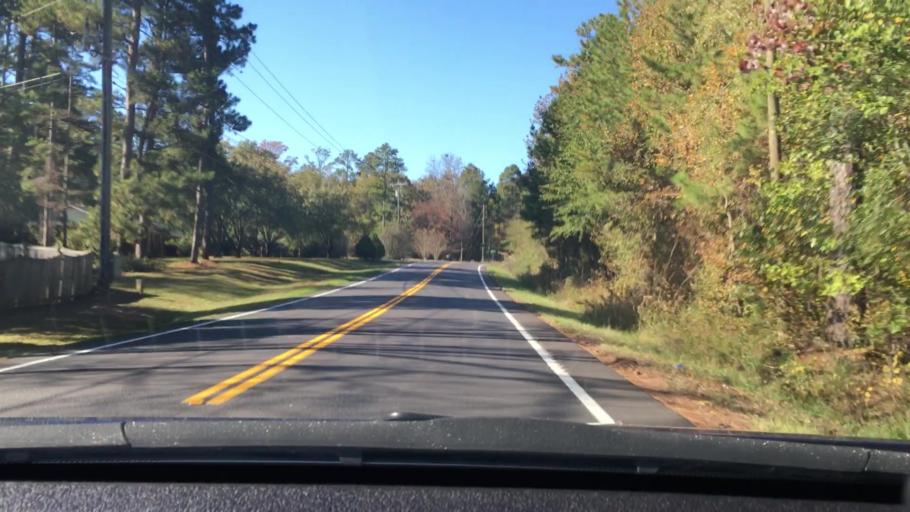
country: US
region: South Carolina
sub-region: Lexington County
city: Irmo
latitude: 34.1250
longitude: -81.1745
